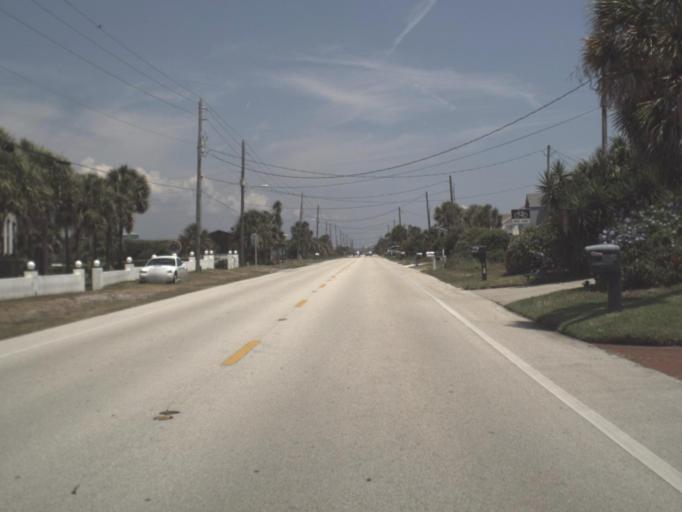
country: US
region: Florida
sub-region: Saint Johns County
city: Villano Beach
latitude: 29.9257
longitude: -81.2953
